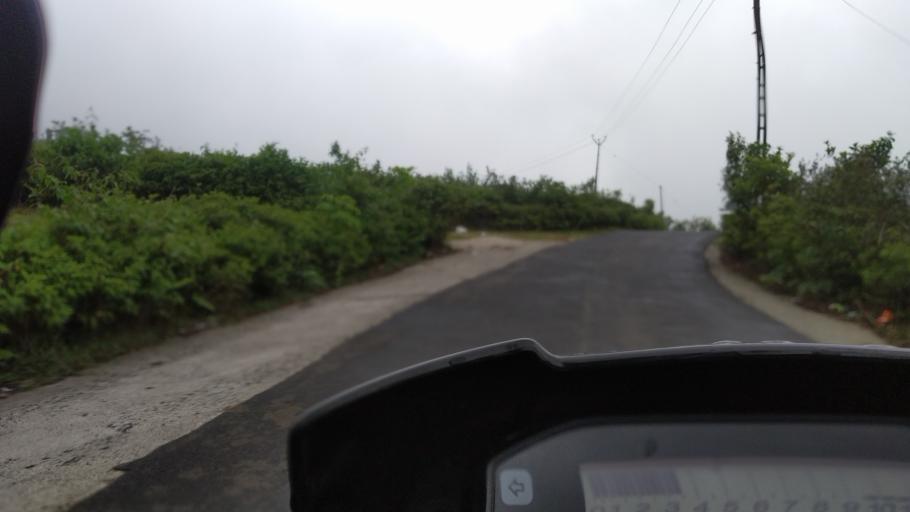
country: IN
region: Kerala
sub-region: Kottayam
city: Erattupetta
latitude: 9.6368
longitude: 76.9346
